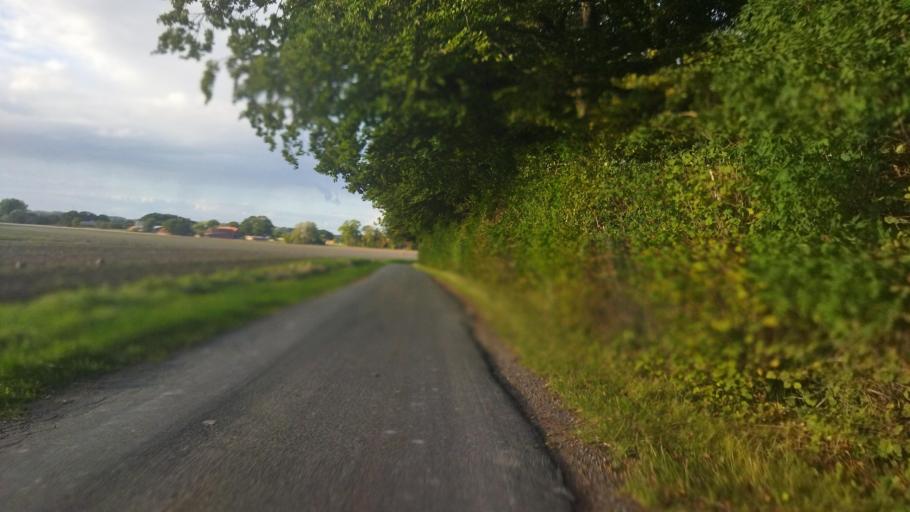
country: DE
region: North Rhine-Westphalia
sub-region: Regierungsbezirk Munster
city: Billerbeck
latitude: 51.9606
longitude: 7.2595
